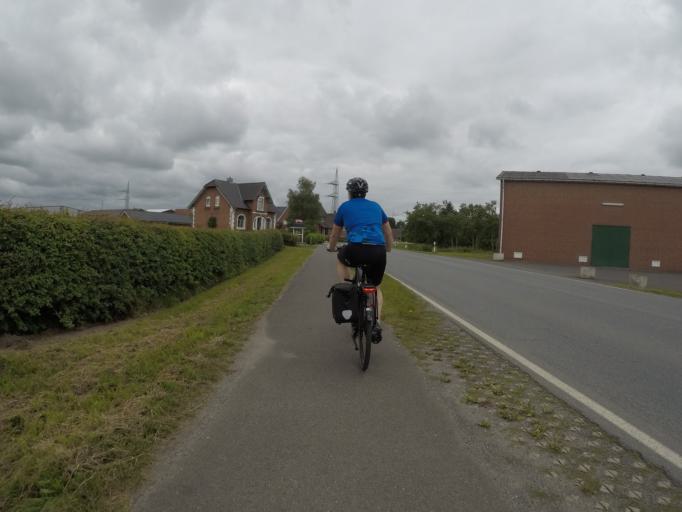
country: DE
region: Schleswig-Holstein
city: Haseldorf
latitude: 53.5912
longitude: 9.5652
